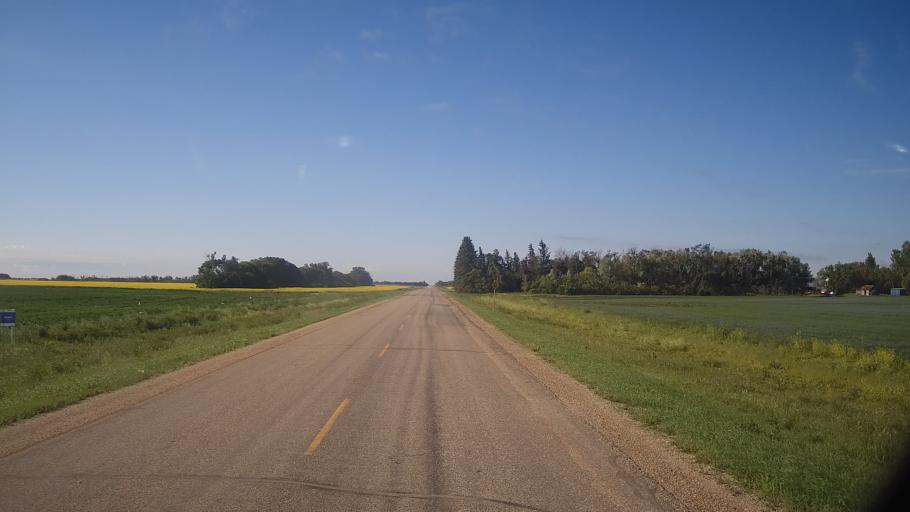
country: CA
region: Saskatchewan
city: Watrous
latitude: 51.8180
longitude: -105.2866
